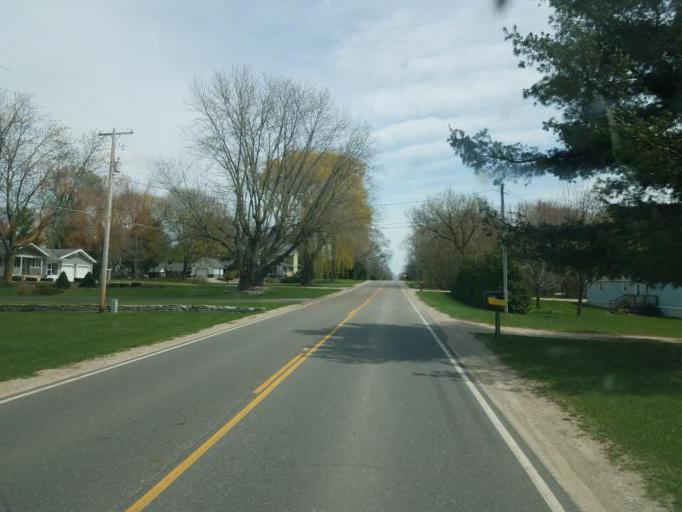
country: US
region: Michigan
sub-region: Isabella County
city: Mount Pleasant
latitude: 43.6259
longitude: -84.8192
